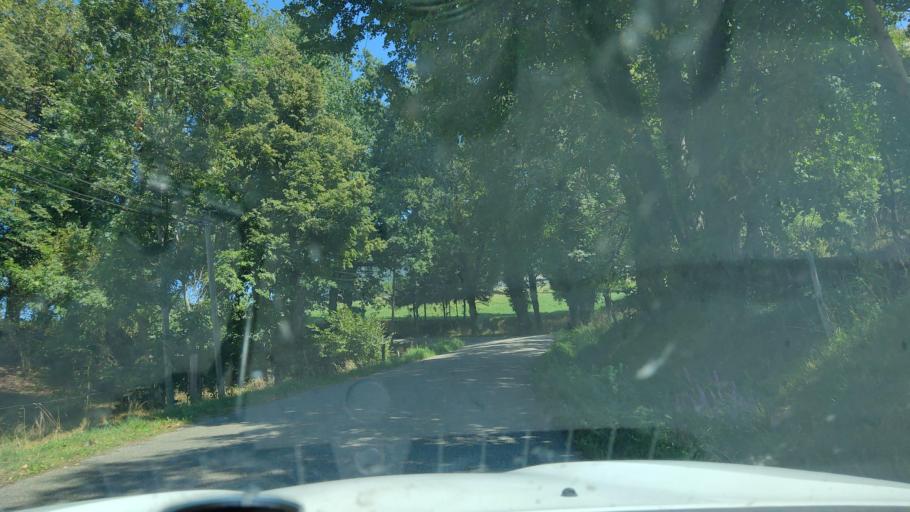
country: FR
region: Rhone-Alpes
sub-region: Departement de la Savoie
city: Novalaise
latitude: 45.6400
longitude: 5.7746
